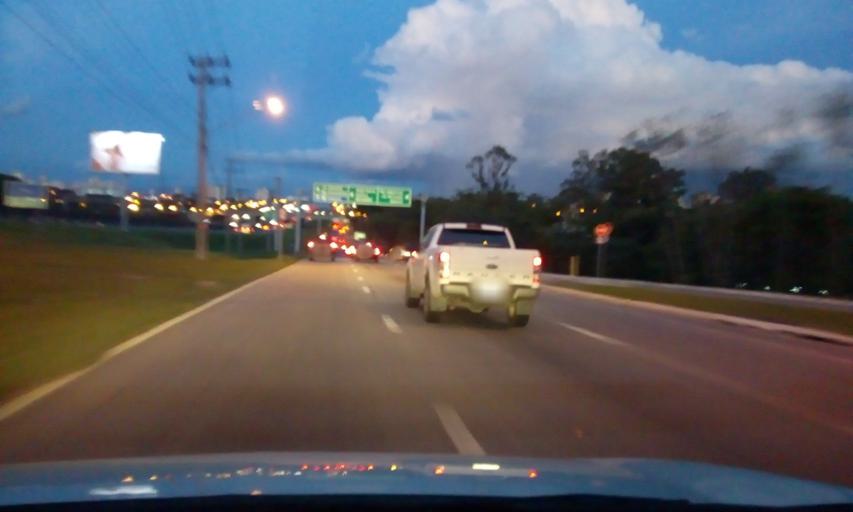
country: BR
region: Sao Paulo
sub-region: Sao Jose Dos Campos
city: Sao Jose dos Campos
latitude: -23.2245
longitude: -45.9046
